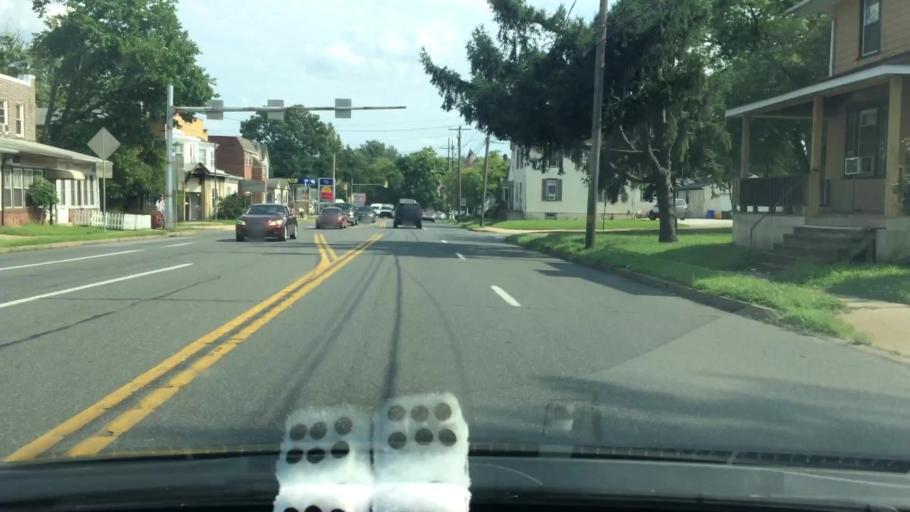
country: US
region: Pennsylvania
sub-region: Delaware County
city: Prospect Park
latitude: 39.8818
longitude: -75.3055
